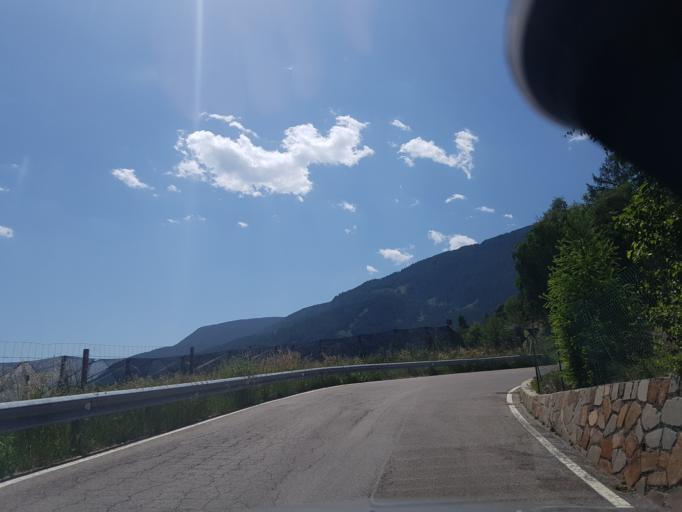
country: IT
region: Trentino-Alto Adige
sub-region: Bolzano
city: Villandro - Villanders
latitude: 46.6278
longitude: 11.5253
